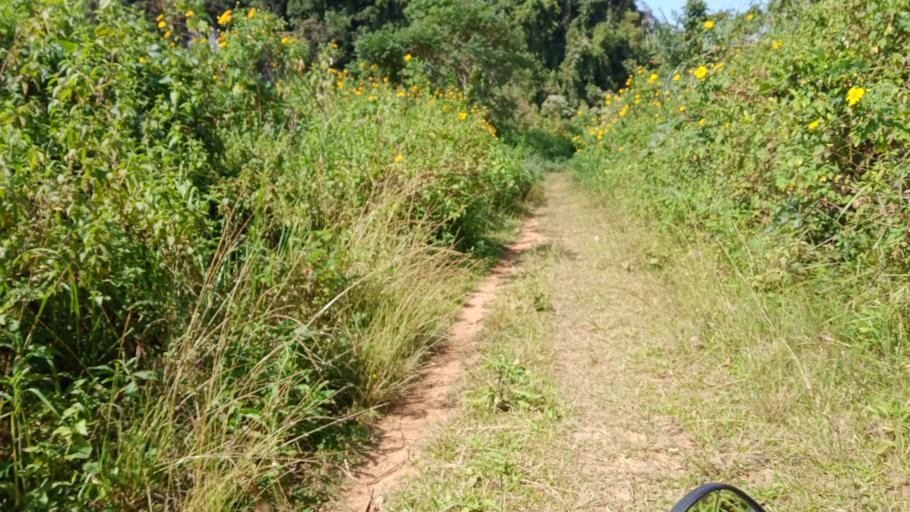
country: LA
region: Xiangkhoang
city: Phonsavan
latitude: 19.1174
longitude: 102.9182
